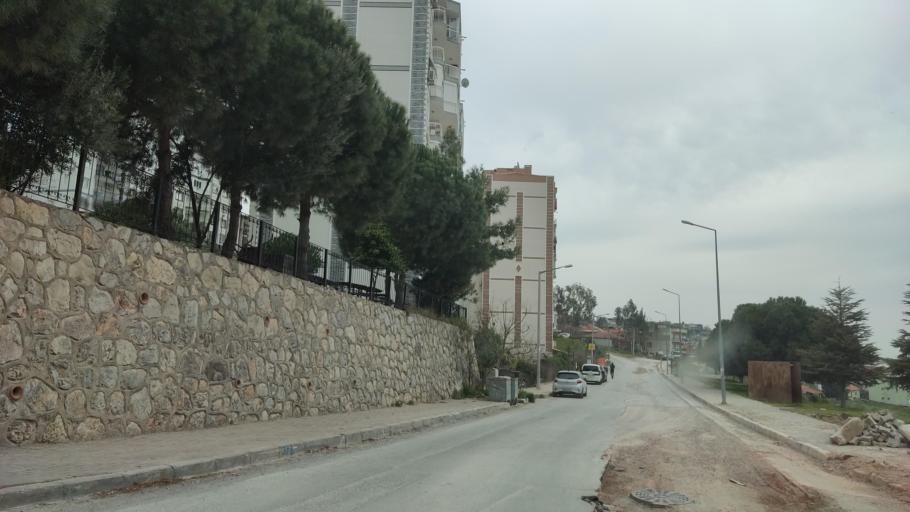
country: TR
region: Izmir
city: Karsiyaka
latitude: 38.5051
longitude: 27.0775
